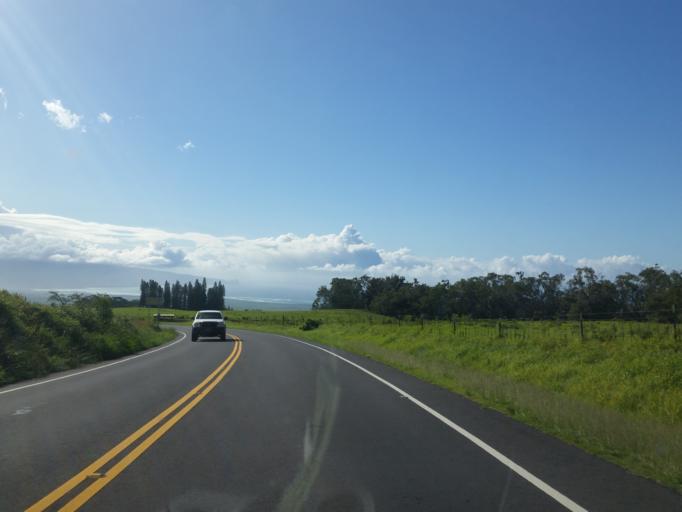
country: US
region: Hawaii
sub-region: Maui County
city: Pukalani
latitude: 20.8202
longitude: -156.3077
